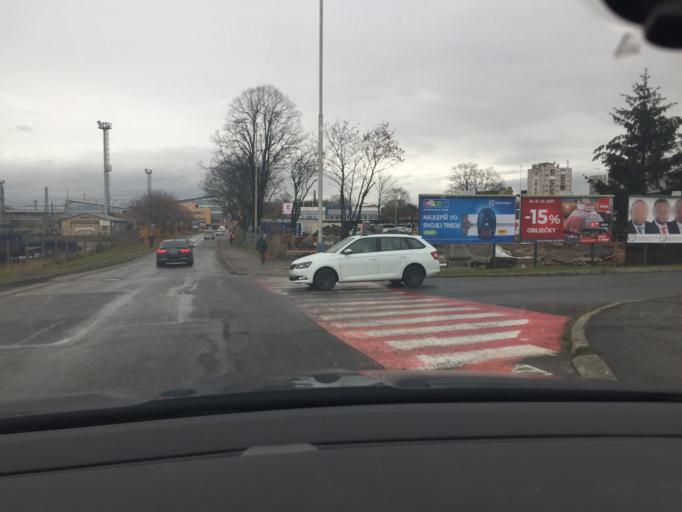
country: SK
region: Presovsky
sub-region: Okres Poprad
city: Poprad
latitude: 49.0600
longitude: 20.2892
